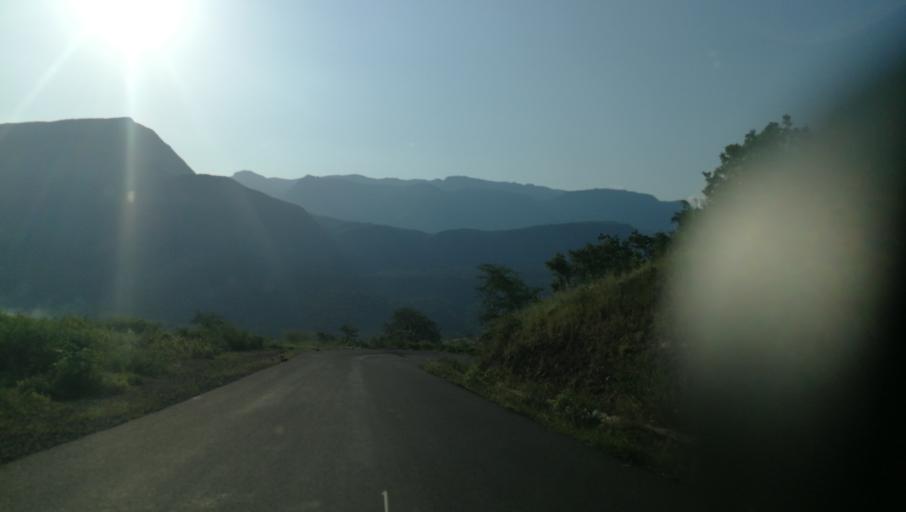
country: ET
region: Southern Nations, Nationalities, and People's Region
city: Areka
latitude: 6.8250
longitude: 37.2991
